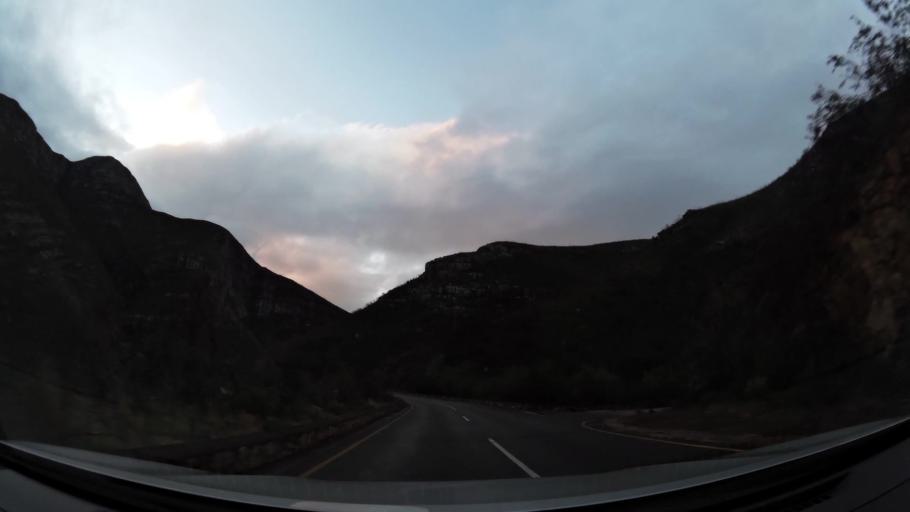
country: ZA
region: Western Cape
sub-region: Overberg District Municipality
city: Swellendam
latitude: -33.9659
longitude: 20.7044
